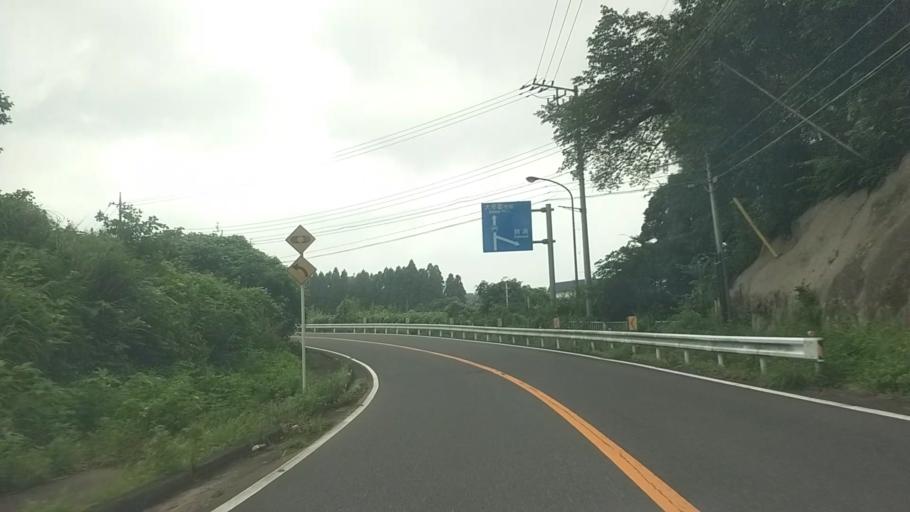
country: JP
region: Chiba
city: Katsuura
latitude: 35.2412
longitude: 140.2432
